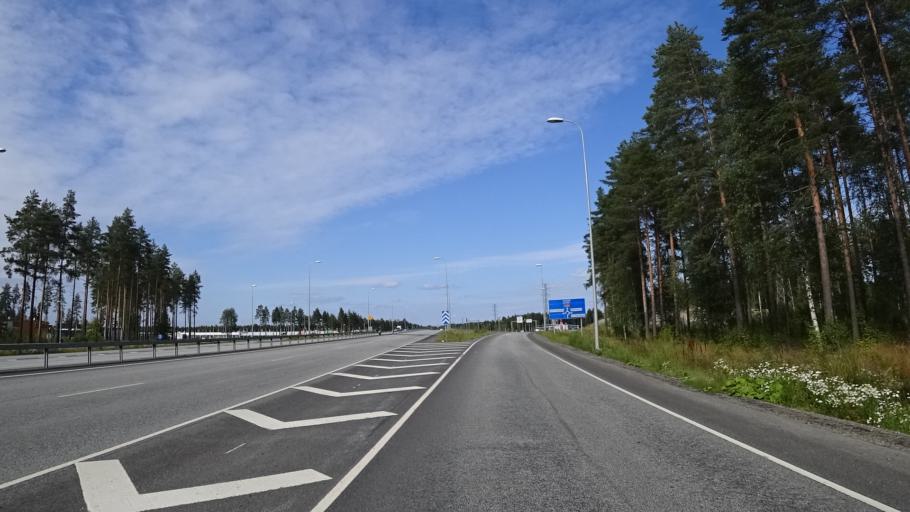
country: FI
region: North Karelia
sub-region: Joensuu
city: Joensuu
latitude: 62.6247
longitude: 29.7779
